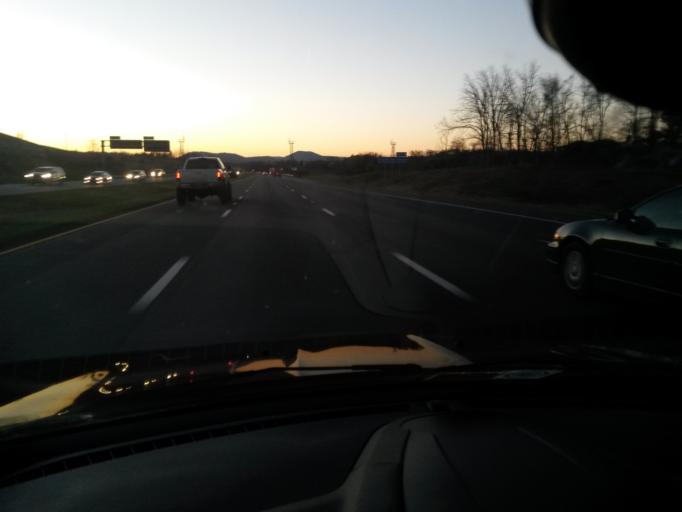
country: US
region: Virginia
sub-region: Roanoke County
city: Hollins
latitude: 37.3237
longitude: -79.9866
